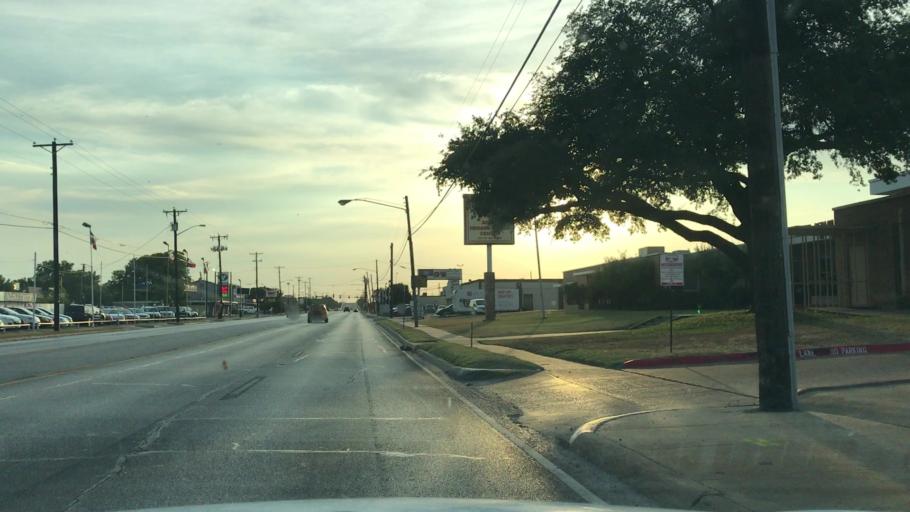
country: US
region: Texas
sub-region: Tarrant County
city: Haltom City
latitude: 32.7952
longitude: -97.3045
